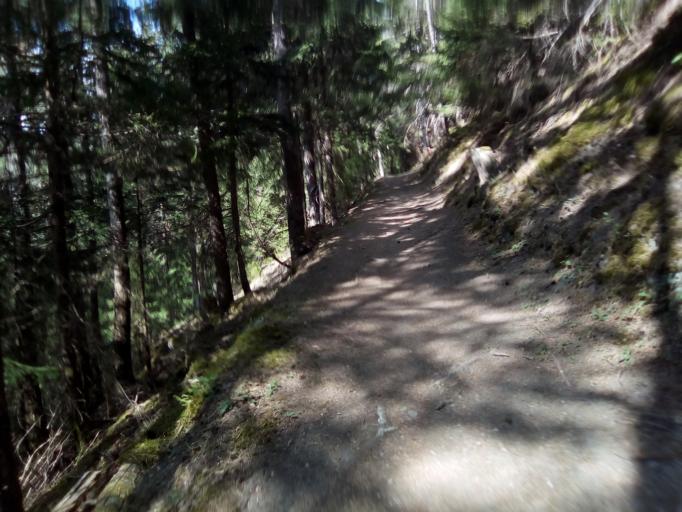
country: CH
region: Valais
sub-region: Entremont District
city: Orsieres
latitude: 46.0418
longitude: 7.1502
